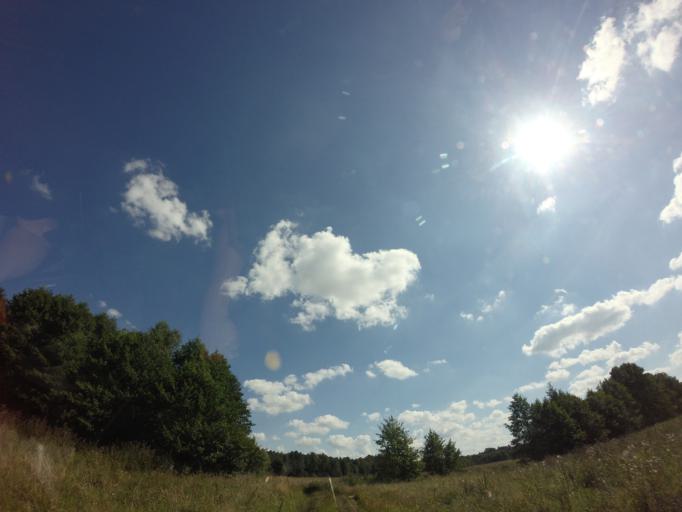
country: PL
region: West Pomeranian Voivodeship
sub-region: Powiat choszczenski
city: Drawno
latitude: 53.2317
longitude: 15.6547
